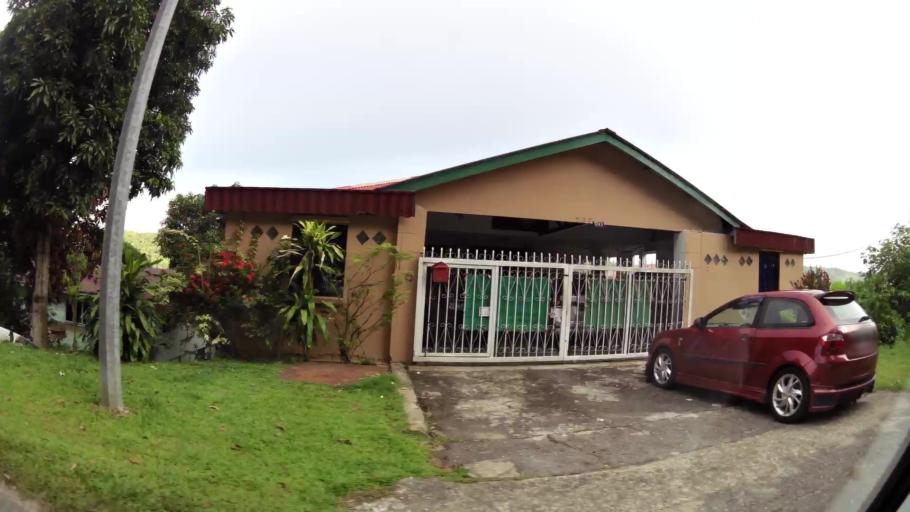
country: BN
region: Brunei and Muara
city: Bandar Seri Begawan
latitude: 4.9005
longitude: 114.9889
